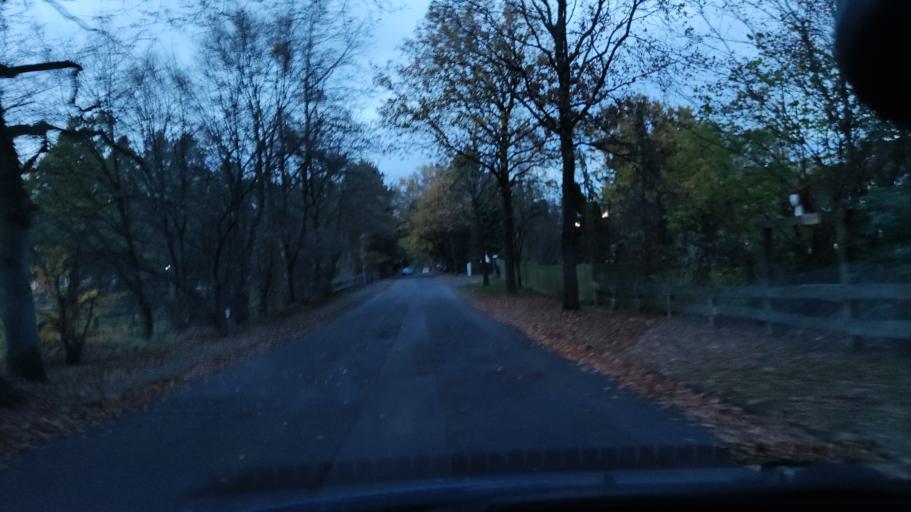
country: DE
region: Lower Saxony
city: Egestorf
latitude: 53.1604
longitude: 10.0349
